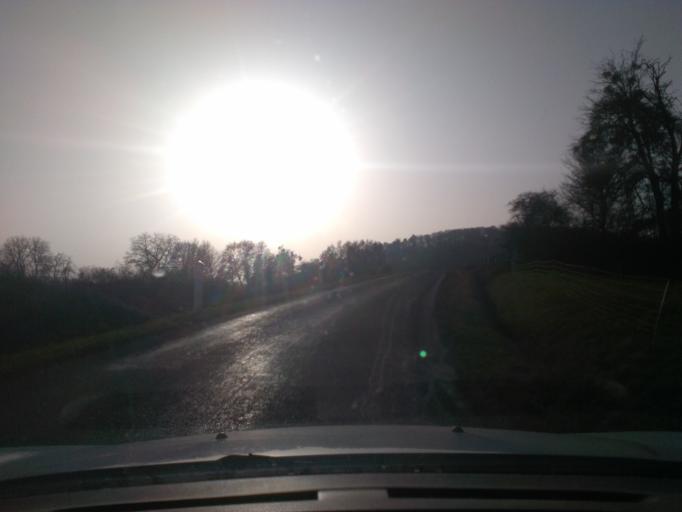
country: FR
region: Lorraine
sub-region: Departement des Vosges
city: Vittel
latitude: 48.2595
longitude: 6.0059
